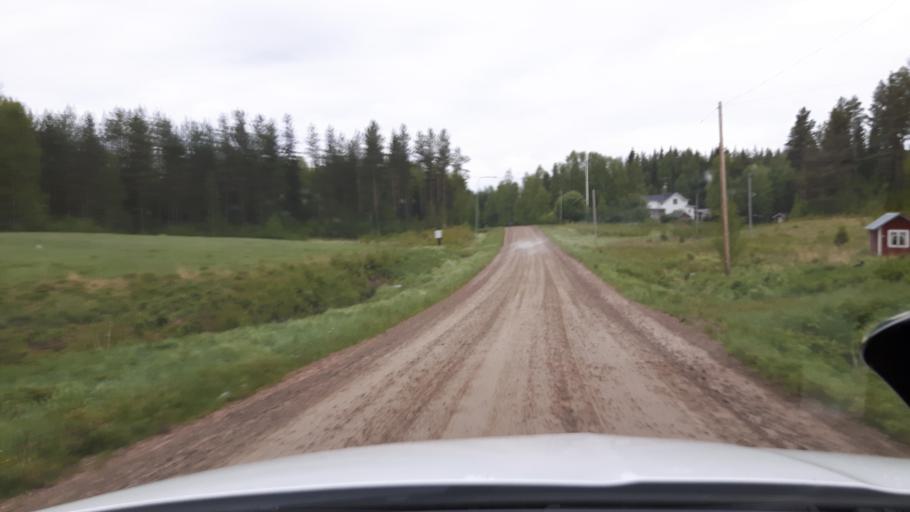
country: SE
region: Vaesternorrland
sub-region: Ange Kommun
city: Ange
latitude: 62.1470
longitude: 15.6613
